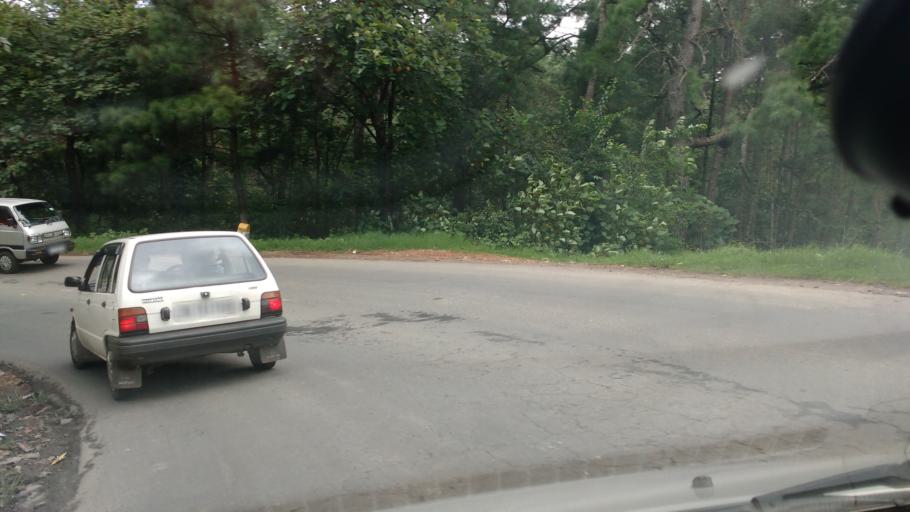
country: IN
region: Meghalaya
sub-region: East Khasi Hills
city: Shillong
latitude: 25.5599
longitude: 91.8521
